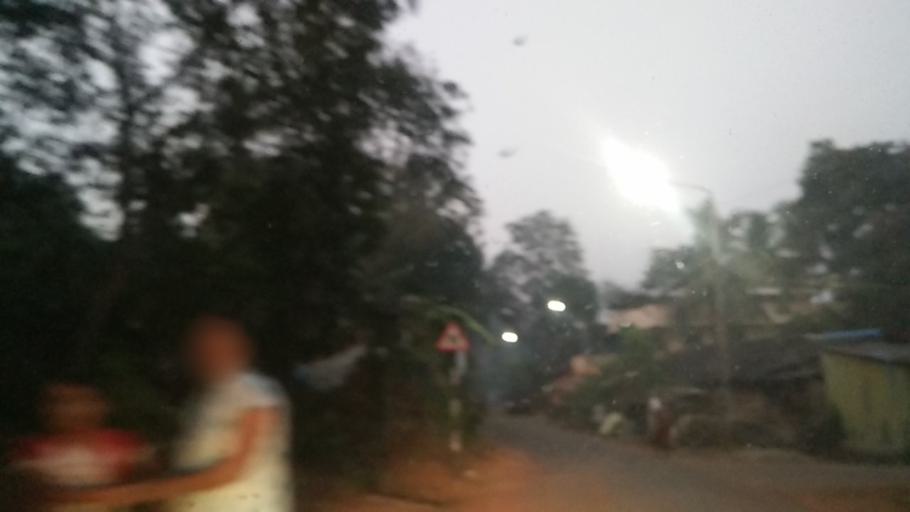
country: IN
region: Goa
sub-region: South Goa
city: Madgaon
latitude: 15.2790
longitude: 73.9685
